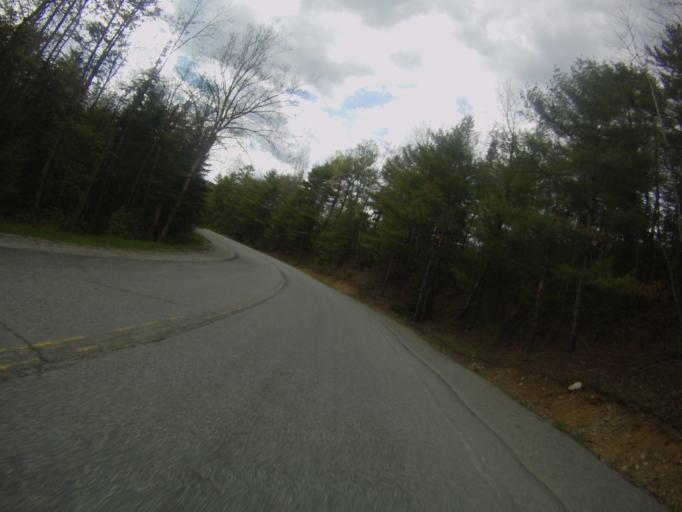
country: US
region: New York
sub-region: Essex County
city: Mineville
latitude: 44.0749
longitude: -73.6367
